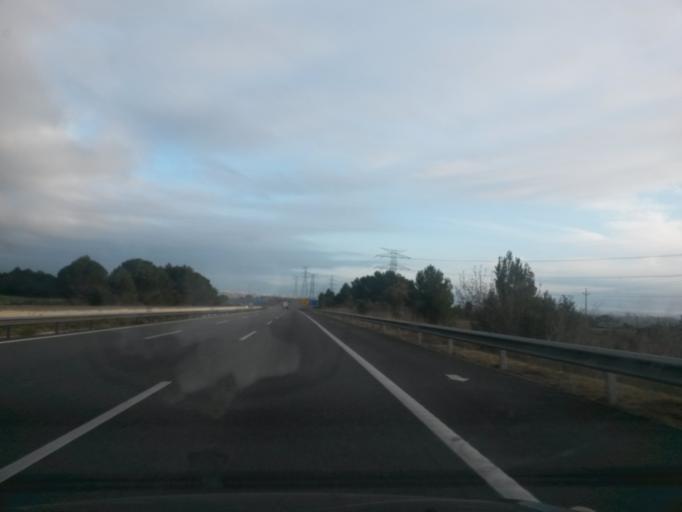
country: ES
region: Catalonia
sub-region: Provincia de Girona
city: Garrigas
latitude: 42.2049
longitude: 2.9373
